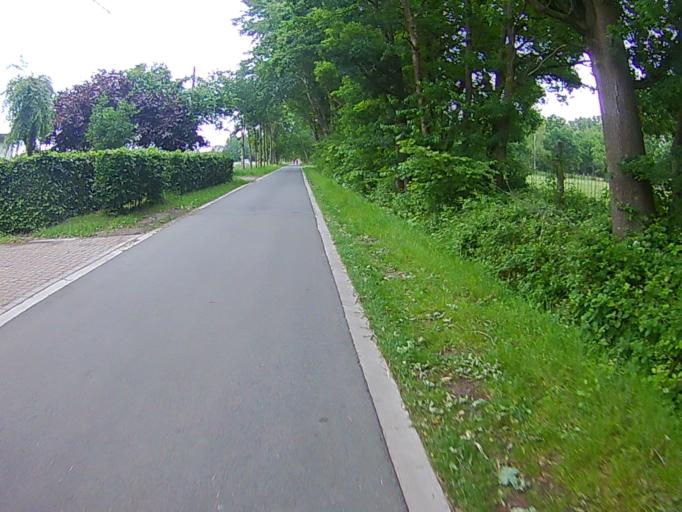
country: BE
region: Flanders
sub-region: Provincie Antwerpen
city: Putte
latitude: 51.0297
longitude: 4.6426
